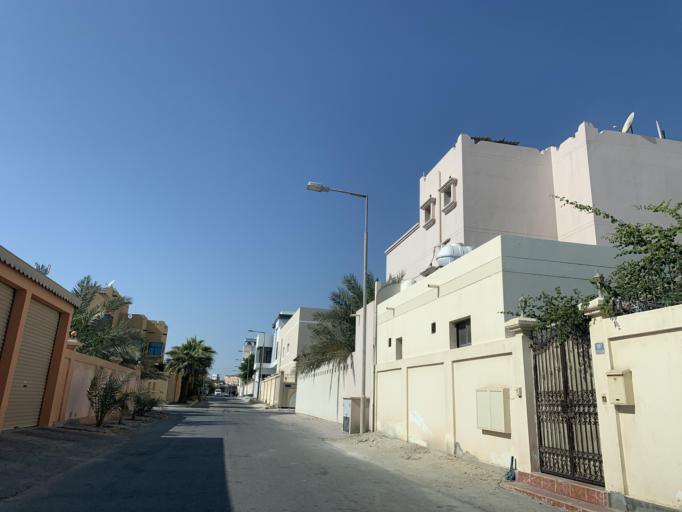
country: BH
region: Central Governorate
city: Madinat Hamad
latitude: 26.1282
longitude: 50.4801
